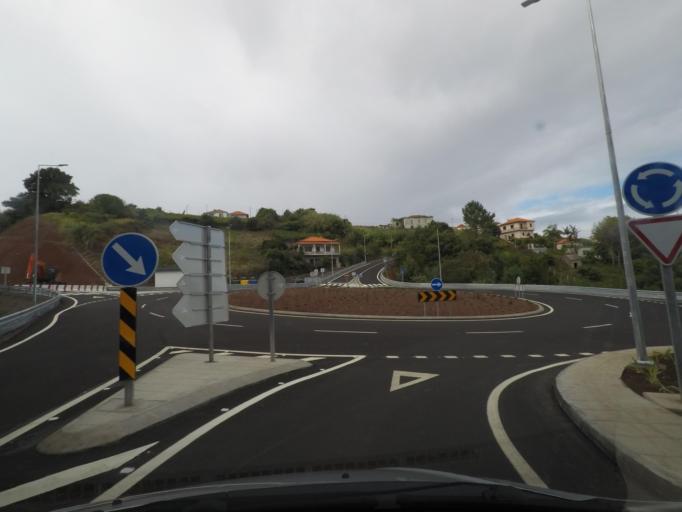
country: PT
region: Madeira
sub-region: Santana
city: Santana
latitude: 32.8300
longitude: -16.9078
